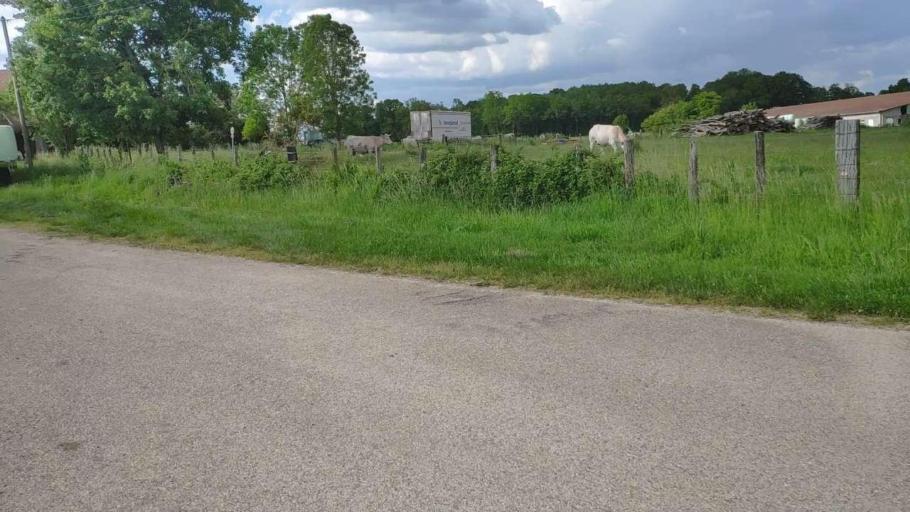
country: FR
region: Bourgogne
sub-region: Departement de Saone-et-Loire
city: Saint-Germain-du-Bois
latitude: 46.8038
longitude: 5.3479
